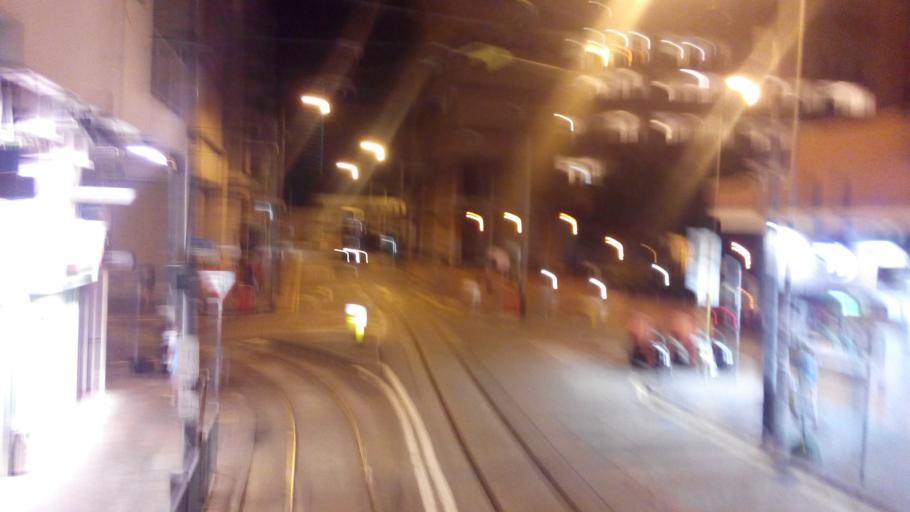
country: HK
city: Hong Kong
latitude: 22.2831
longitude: 114.1271
